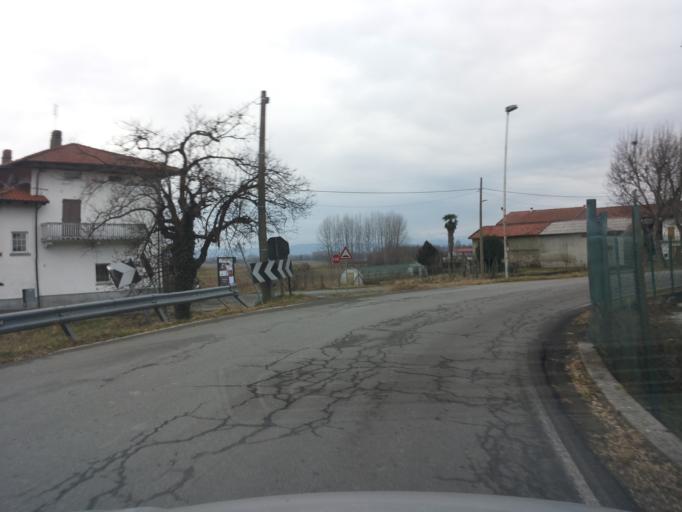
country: IT
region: Piedmont
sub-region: Provincia di Torino
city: Borgomasino
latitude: 45.3656
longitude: 7.9852
